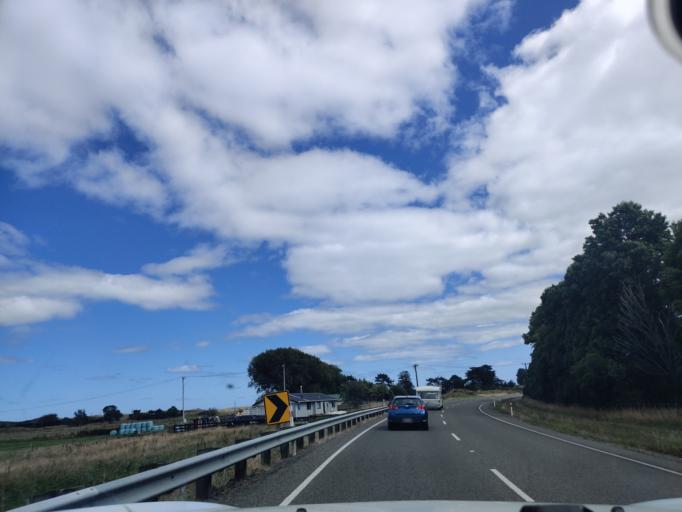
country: NZ
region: Manawatu-Wanganui
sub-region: Horowhenua District
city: Foxton
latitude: -40.4199
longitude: 175.4120
